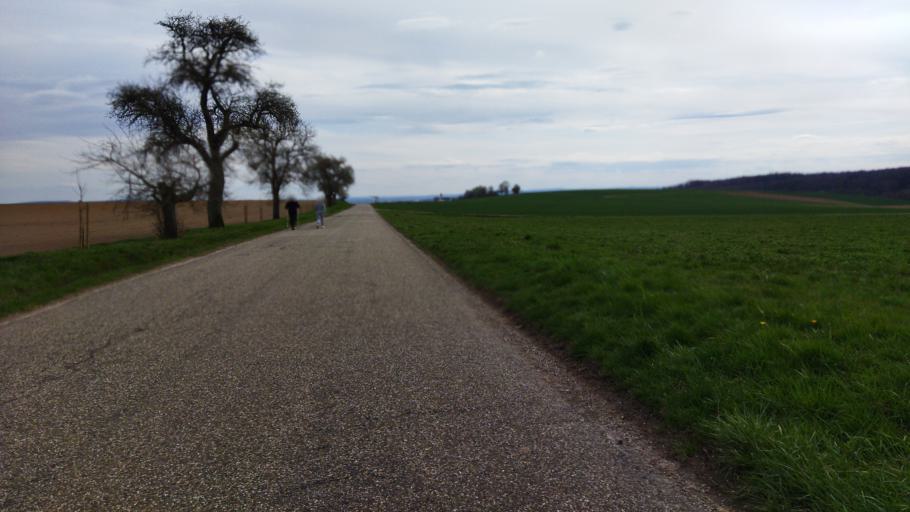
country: DE
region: Baden-Wuerttemberg
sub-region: Regierungsbezirk Stuttgart
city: Neudenau
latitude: 49.2979
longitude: 9.2280
